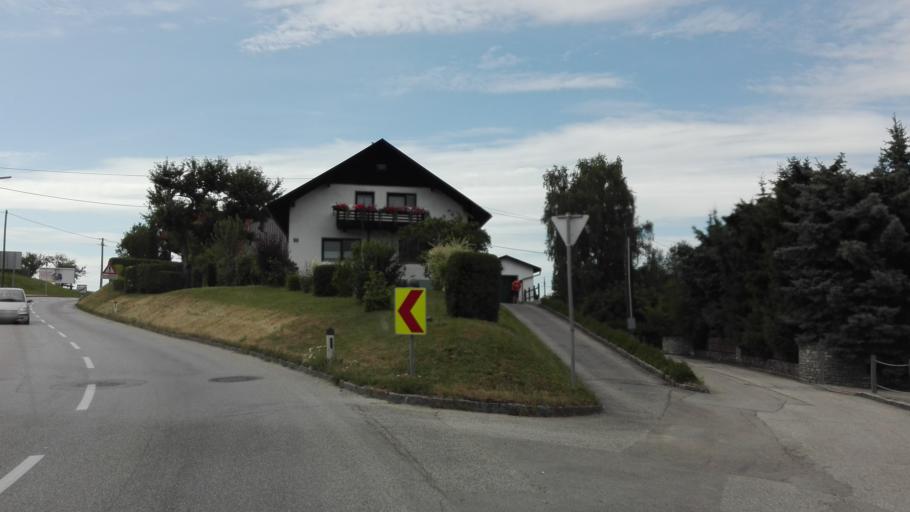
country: AT
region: Upper Austria
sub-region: Politischer Bezirk Grieskirchen
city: Grieskirchen
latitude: 48.2391
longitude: 13.8231
